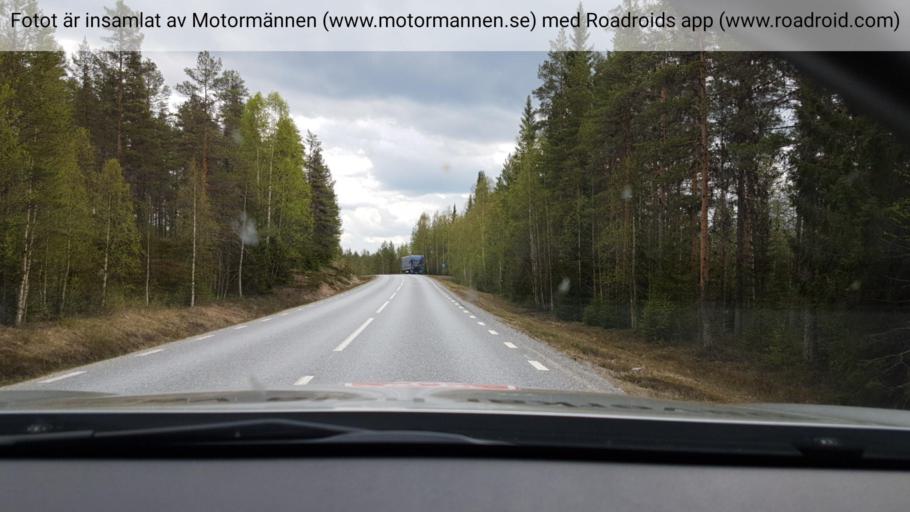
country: SE
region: Vaesterbotten
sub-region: Bjurholms Kommun
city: Bjurholm
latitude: 64.0026
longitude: 18.7328
